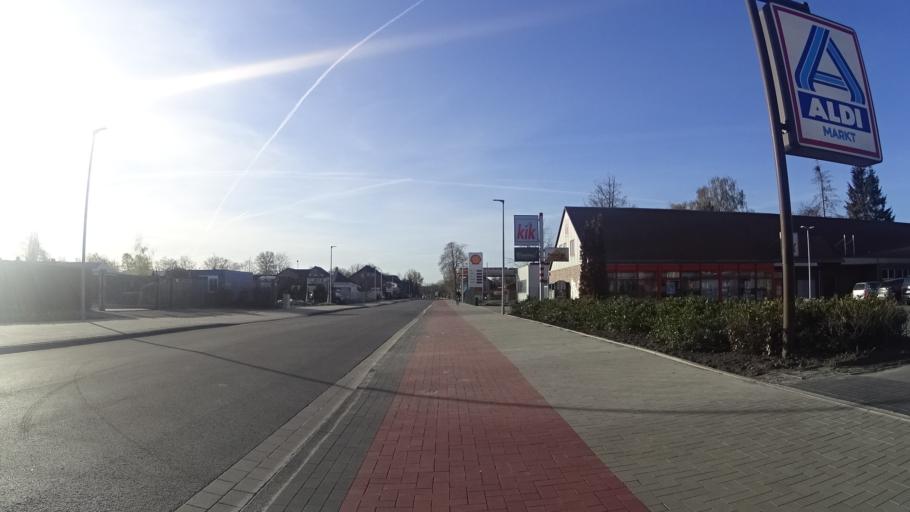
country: DE
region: North Rhine-Westphalia
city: Emsdetten
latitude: 52.1331
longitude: 7.5462
